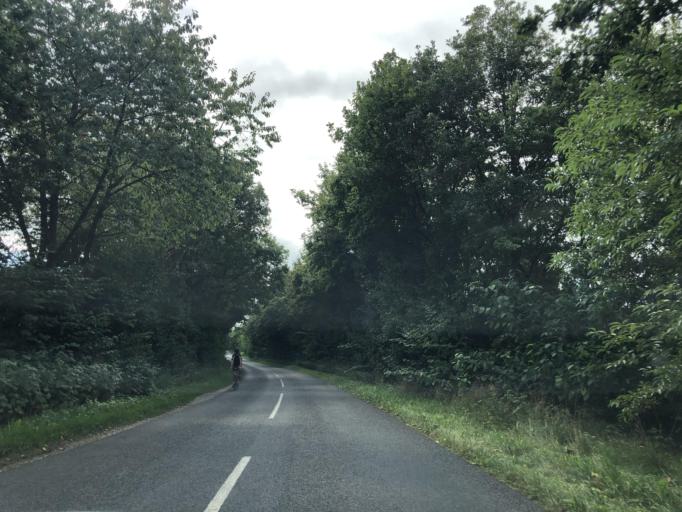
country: DK
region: North Denmark
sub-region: Vesthimmerland Kommune
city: Alestrup
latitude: 56.6030
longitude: 9.4333
